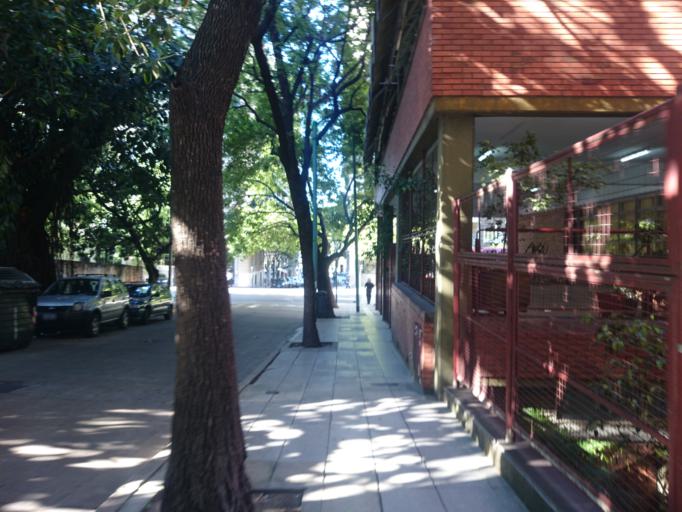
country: AR
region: Buenos Aires F.D.
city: Retiro
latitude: -34.5933
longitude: -58.3775
